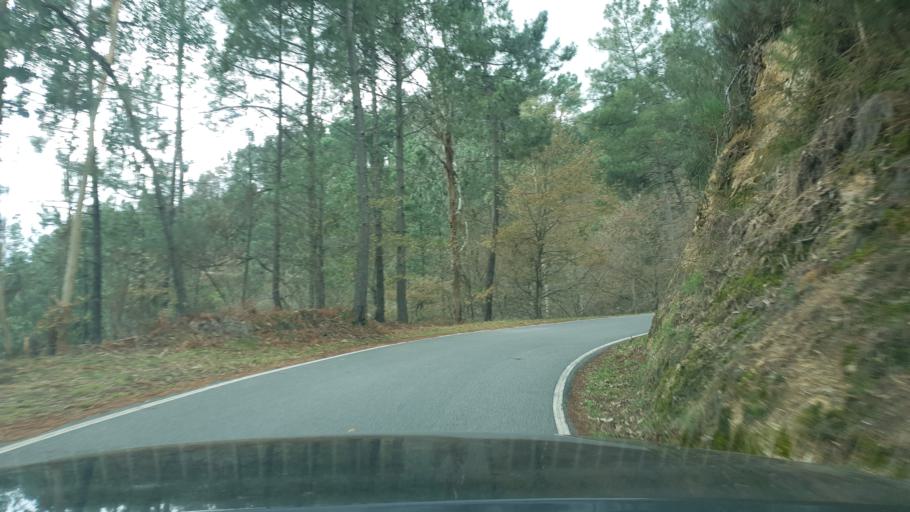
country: PT
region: Viseu
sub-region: Castro Daire
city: Castro Daire
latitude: 40.8862
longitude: -8.0148
